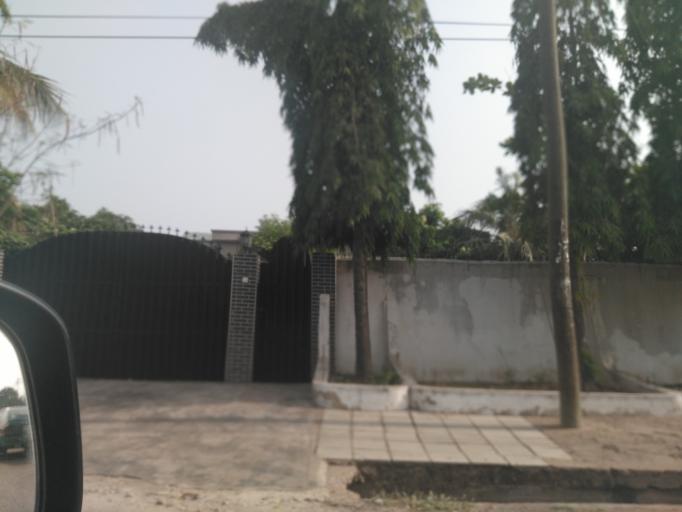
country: GH
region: Greater Accra
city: Accra
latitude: 5.6066
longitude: -0.1977
